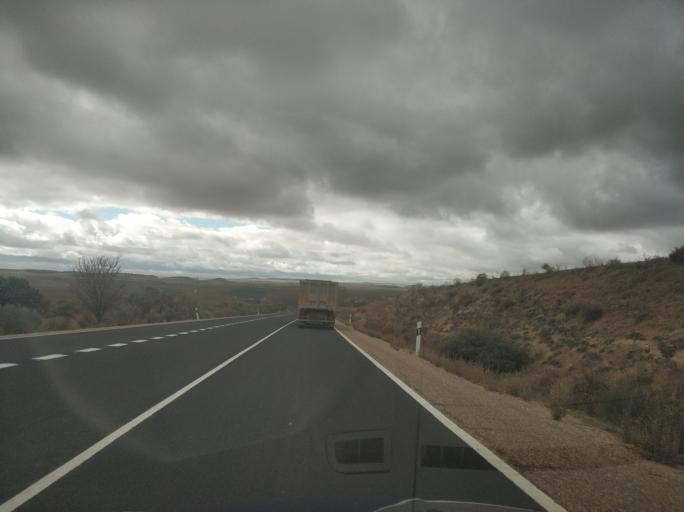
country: ES
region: Castille and Leon
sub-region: Provincia de Zamora
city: Castrillo de la Guarena
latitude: 41.2374
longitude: -5.3005
